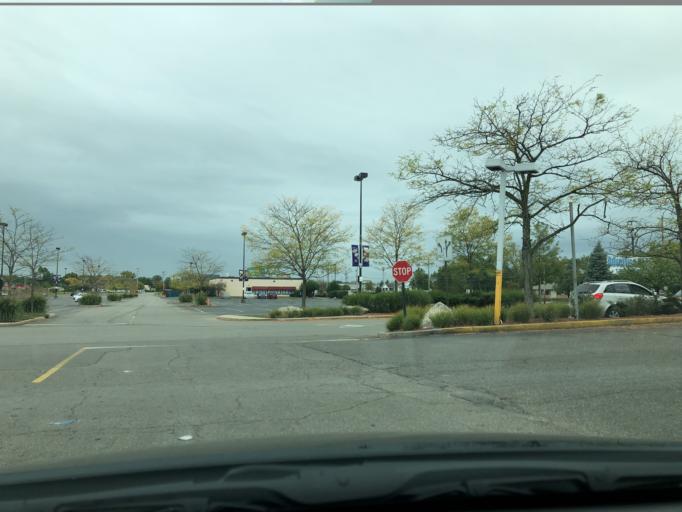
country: US
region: Ohio
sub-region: Franklin County
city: Minerva Park
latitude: 40.0885
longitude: -82.9500
